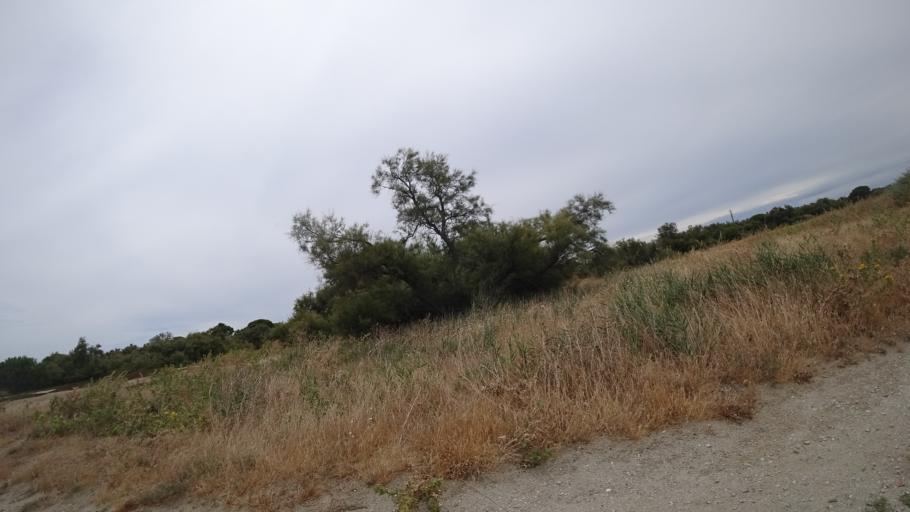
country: FR
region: Languedoc-Roussillon
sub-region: Departement des Pyrenees-Orientales
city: Le Barcares
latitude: 42.8274
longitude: 3.0322
